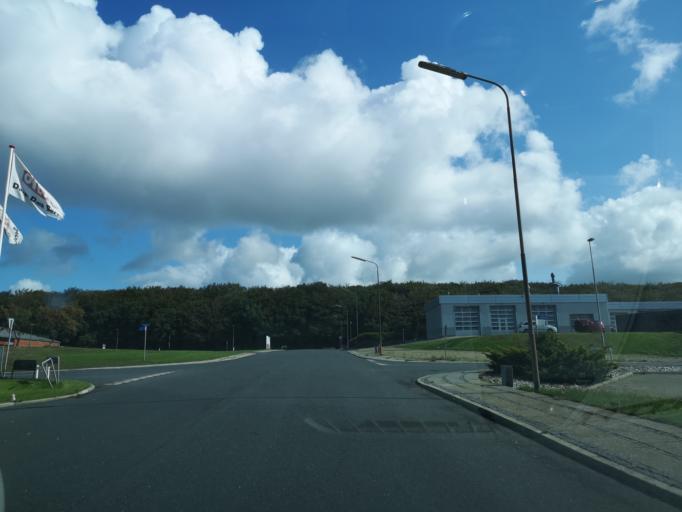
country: DK
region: Central Jutland
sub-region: Holstebro Kommune
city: Holstebro
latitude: 56.3407
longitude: 8.6361
